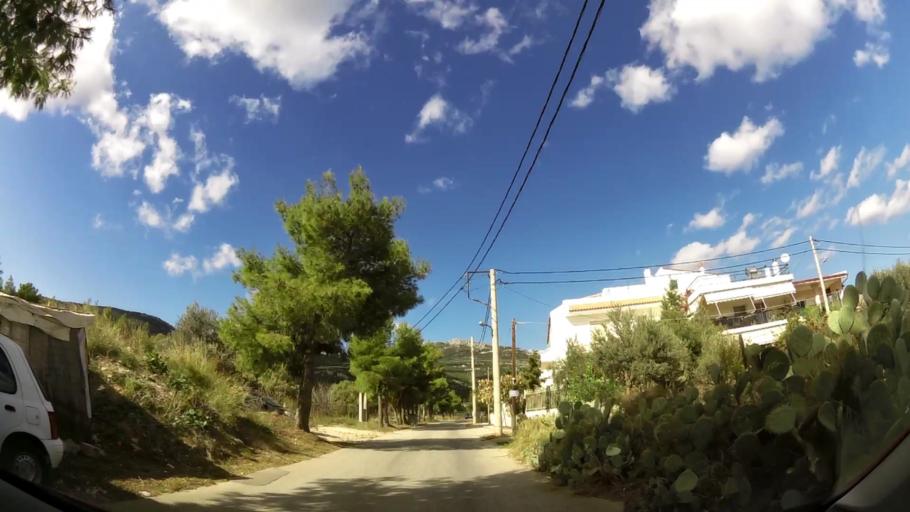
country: GR
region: Attica
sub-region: Nomarchia Anatolikis Attikis
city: Acharnes
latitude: 38.1110
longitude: 23.7317
